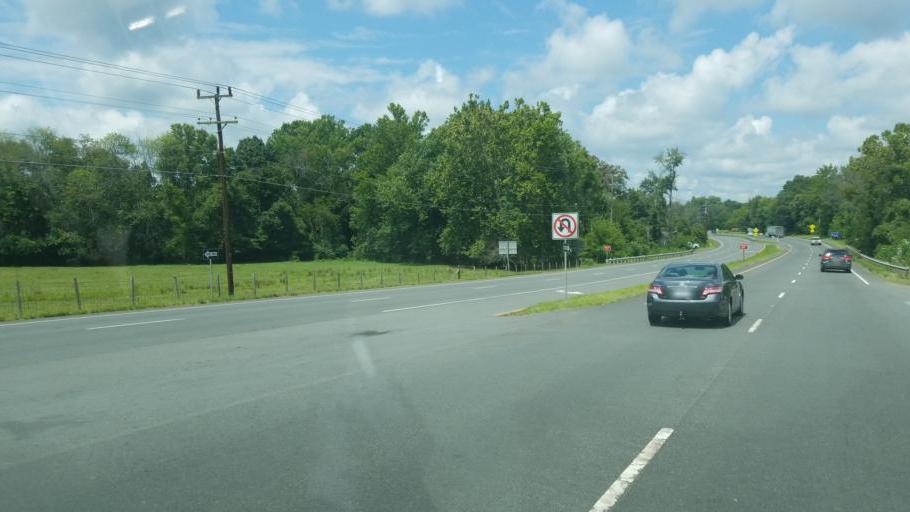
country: US
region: Virginia
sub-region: Fauquier County
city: Bealeton
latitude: 38.6312
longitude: -77.8007
